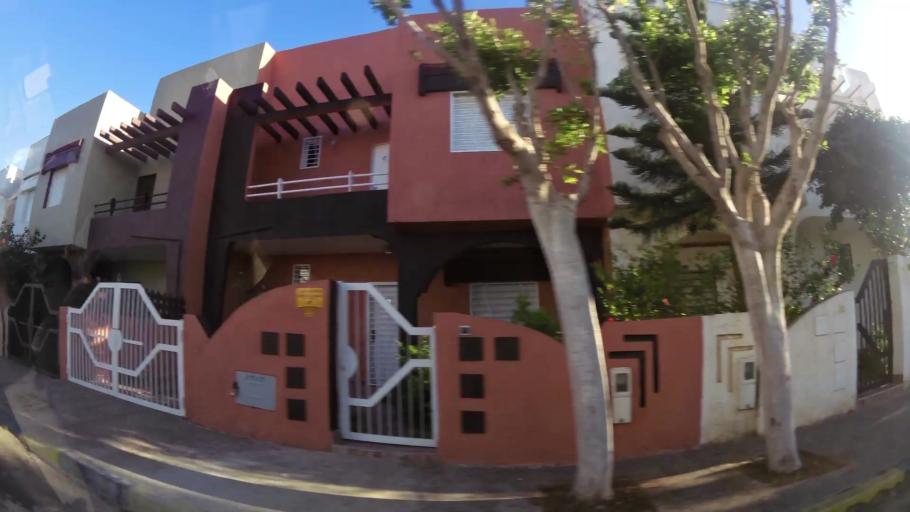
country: MA
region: Oriental
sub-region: Berkane-Taourirt
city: Madagh
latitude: 35.0860
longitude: -2.2508
